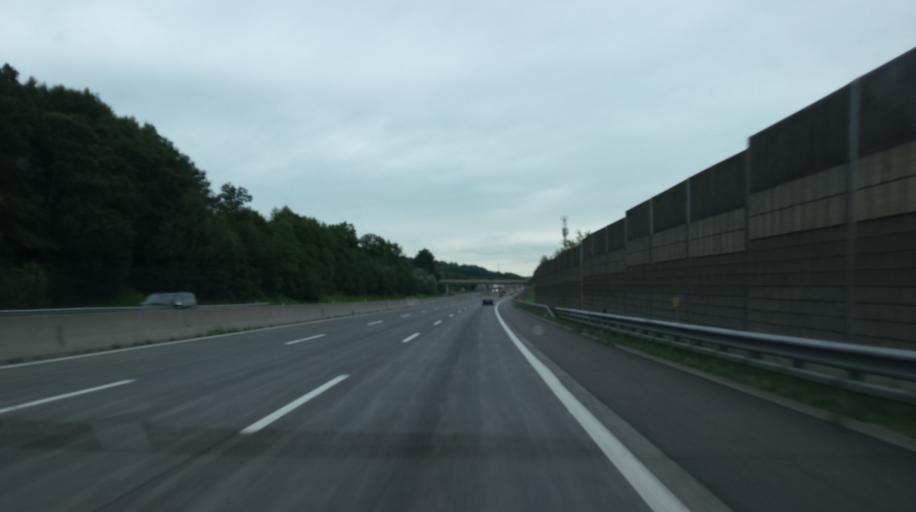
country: AT
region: Lower Austria
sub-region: Politischer Bezirk Melk
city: Blindenmarkt
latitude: 48.1361
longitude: 14.9814
